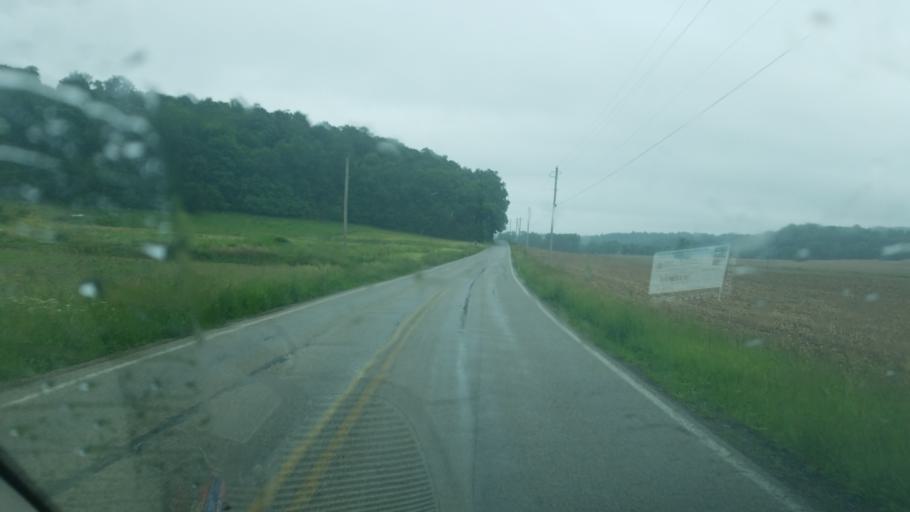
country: US
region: Ohio
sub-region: Sandusky County
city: Bellville
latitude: 40.6769
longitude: -82.4424
